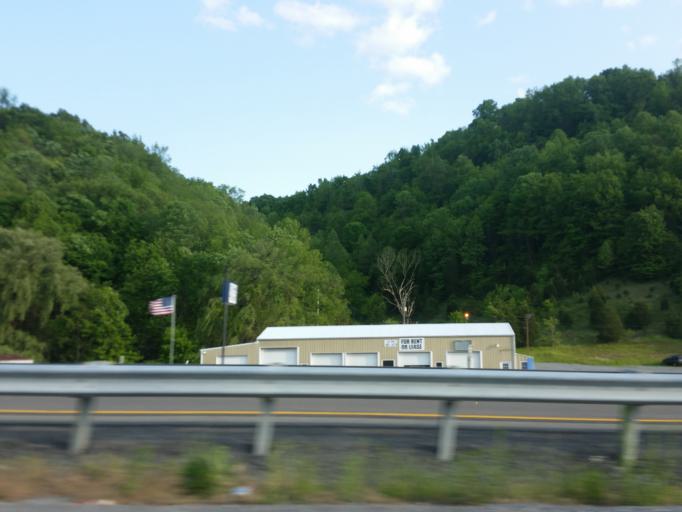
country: US
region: Virginia
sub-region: Russell County
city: Lebanon
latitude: 36.9110
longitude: -82.0251
